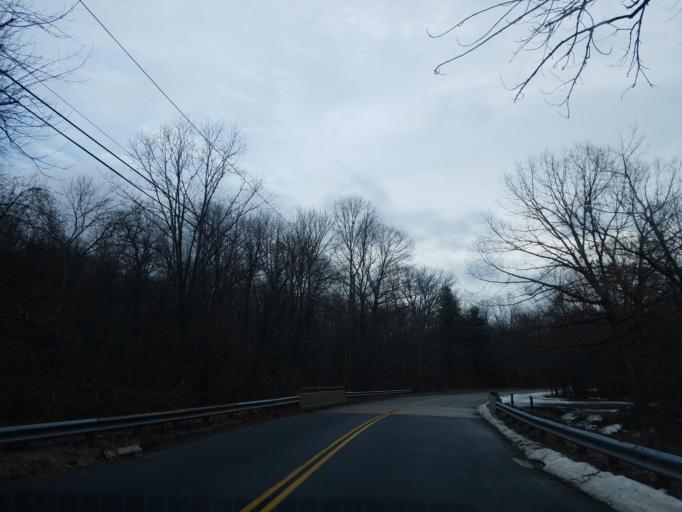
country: US
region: Connecticut
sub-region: Hartford County
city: Glastonbury Center
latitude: 41.6729
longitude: -72.5617
